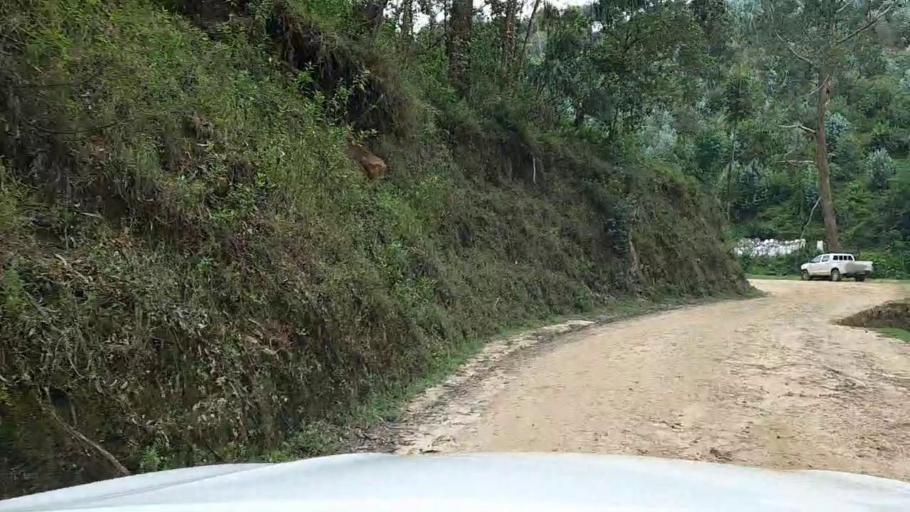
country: RW
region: Western Province
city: Kibuye
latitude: -2.2690
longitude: 29.3620
